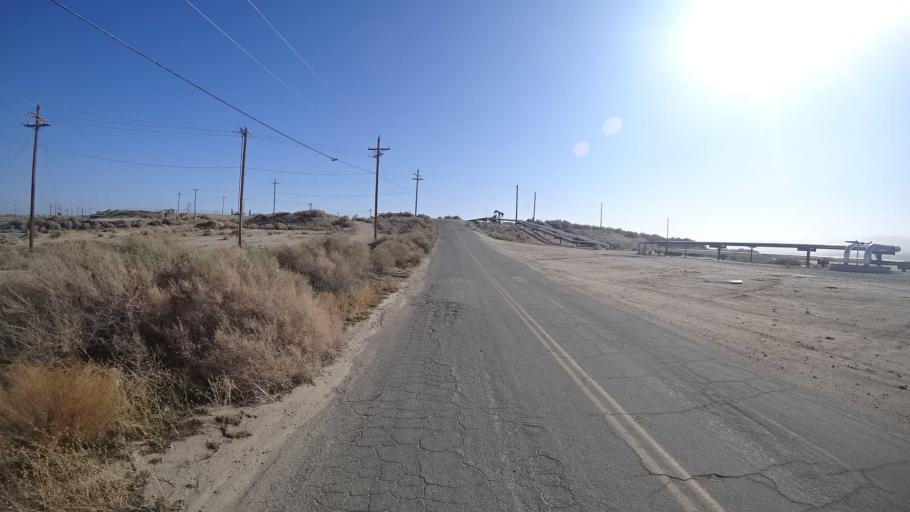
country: US
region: California
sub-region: Kern County
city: Taft Heights
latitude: 35.1142
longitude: -119.4746
